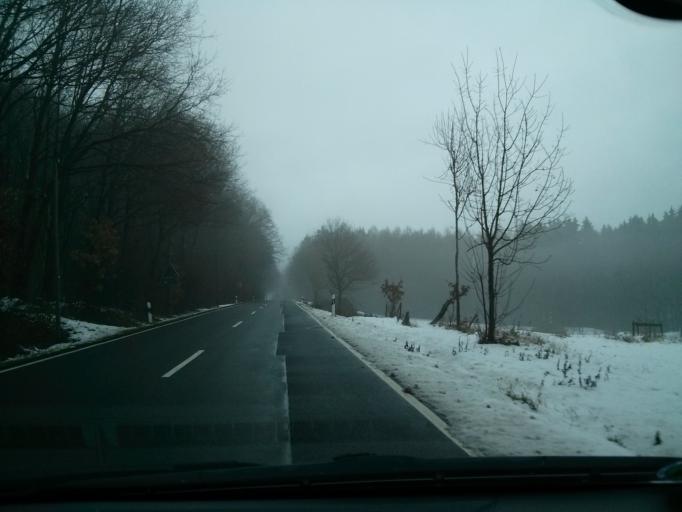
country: DE
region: Rheinland-Pfalz
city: Kalenborn
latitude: 50.5739
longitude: 6.9855
